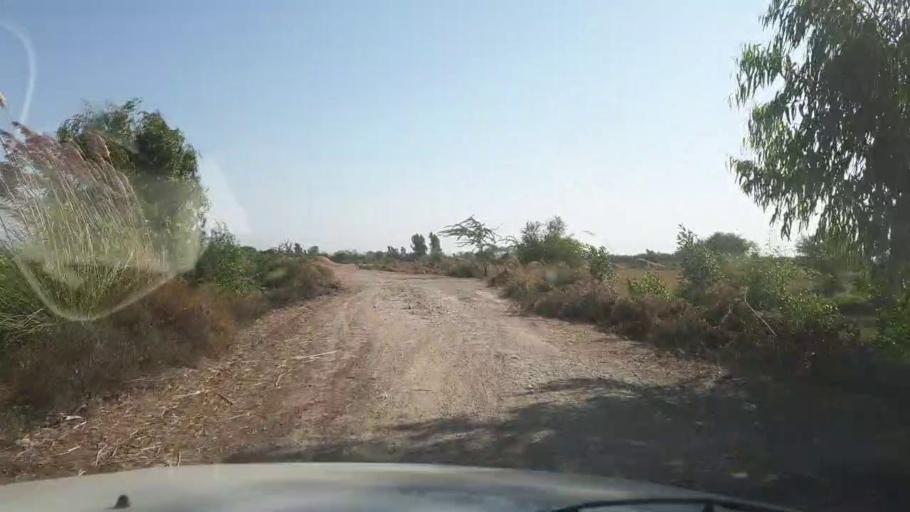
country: PK
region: Sindh
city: Mirpur Sakro
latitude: 24.4860
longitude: 67.8123
